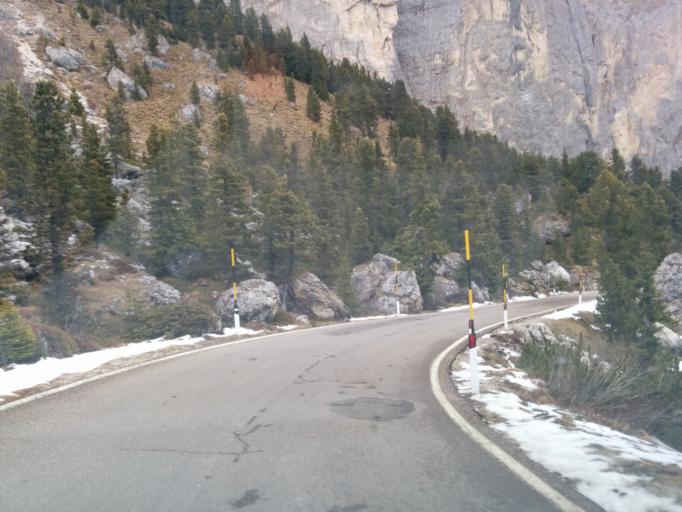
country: IT
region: Trentino-Alto Adige
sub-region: Provincia di Trento
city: Canazei
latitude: 46.5049
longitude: 11.7771
